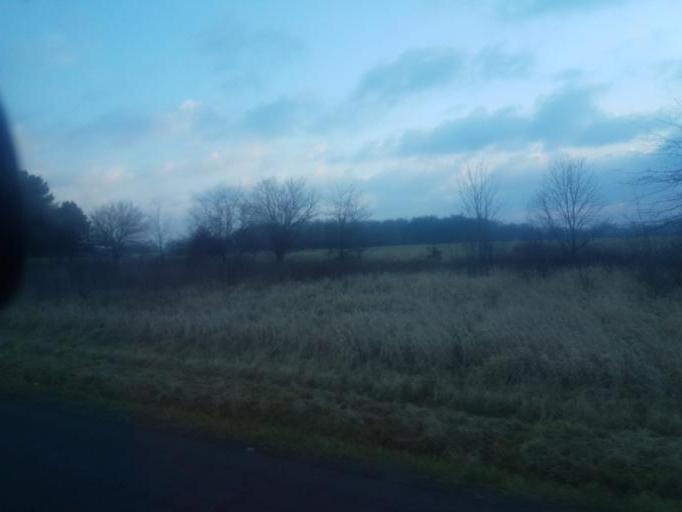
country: US
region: Ohio
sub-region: Marion County
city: Marion
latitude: 40.6207
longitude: -83.1887
